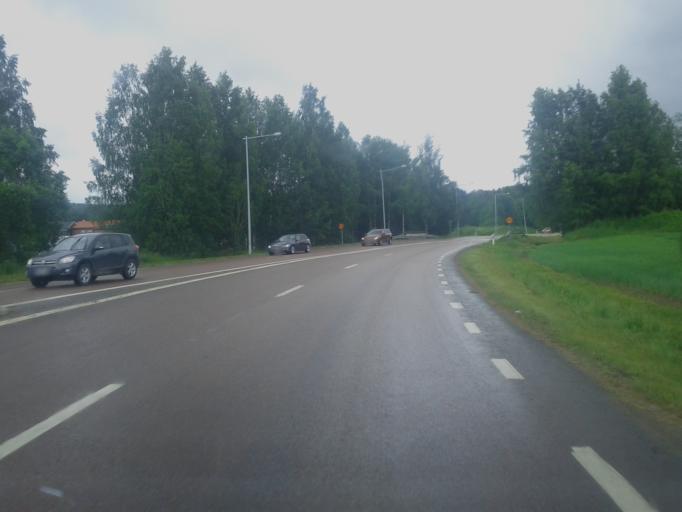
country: SE
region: Vaesternorrland
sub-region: Sundsvalls Kommun
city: Sundsvall
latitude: 62.4123
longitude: 17.2333
